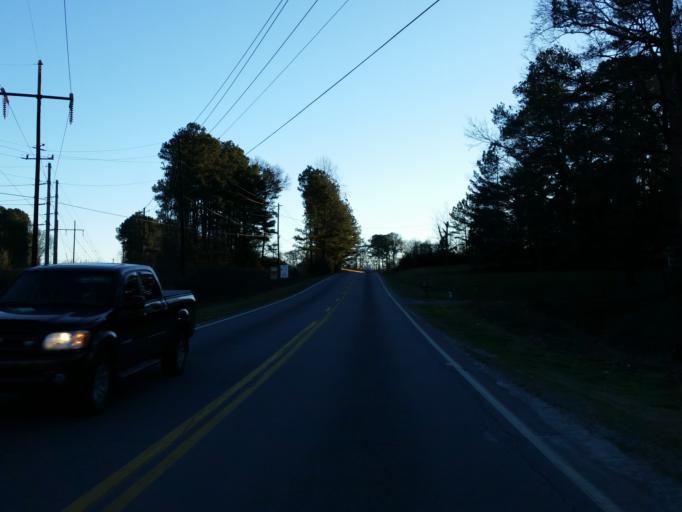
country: US
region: Georgia
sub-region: Cherokee County
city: Woodstock
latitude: 34.1198
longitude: -84.5073
